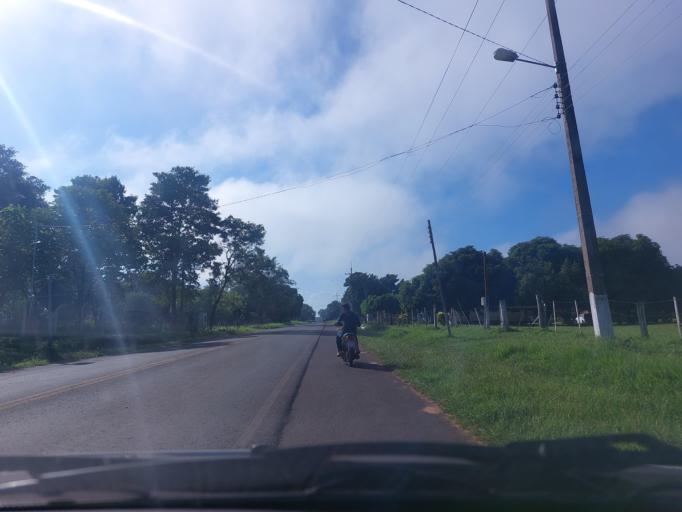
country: PY
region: San Pedro
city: Guayaybi
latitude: -24.5320
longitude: -56.5185
